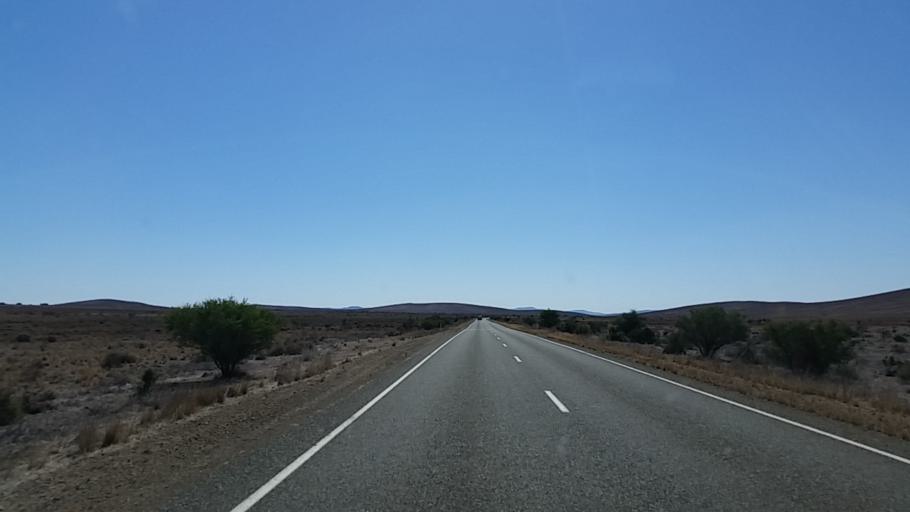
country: AU
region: South Australia
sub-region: Flinders Ranges
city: Quorn
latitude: -32.1552
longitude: 138.5268
